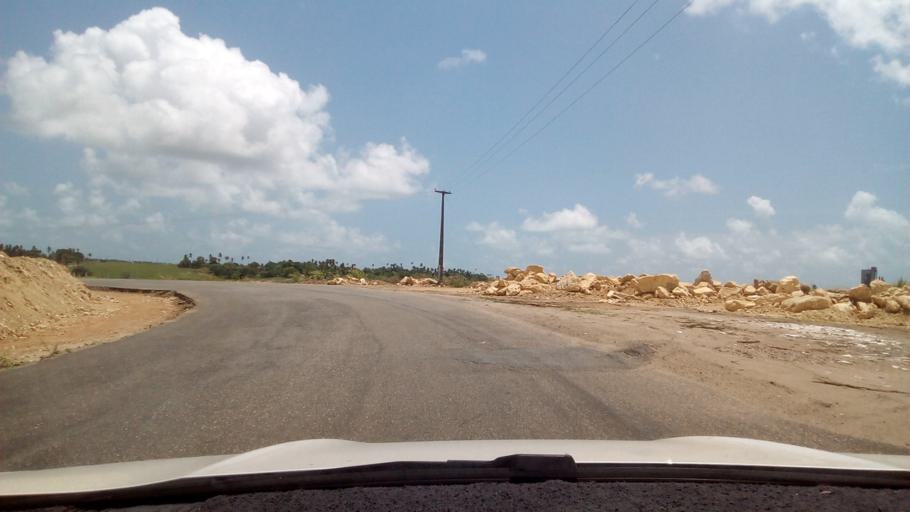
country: BR
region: Paraiba
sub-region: Caapora
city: Caapora
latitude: -7.5189
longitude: -34.8791
